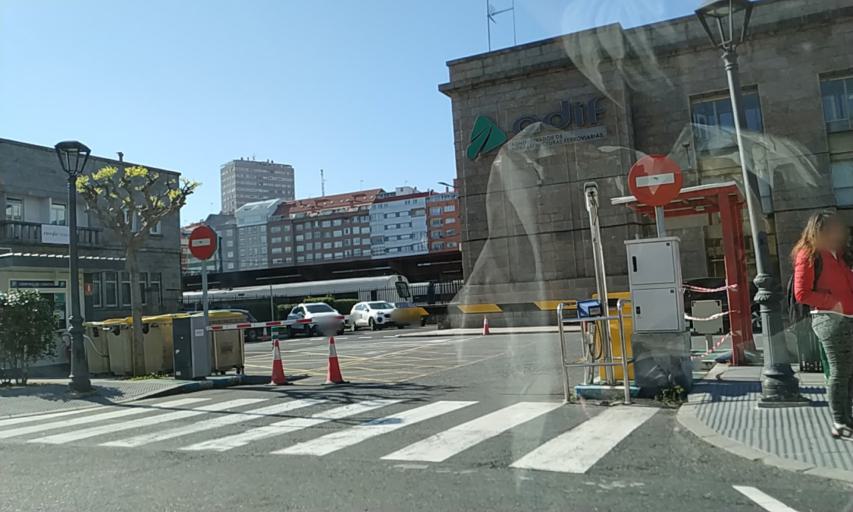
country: ES
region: Galicia
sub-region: Provincia da Coruna
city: A Coruna
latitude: 43.3519
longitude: -8.4097
